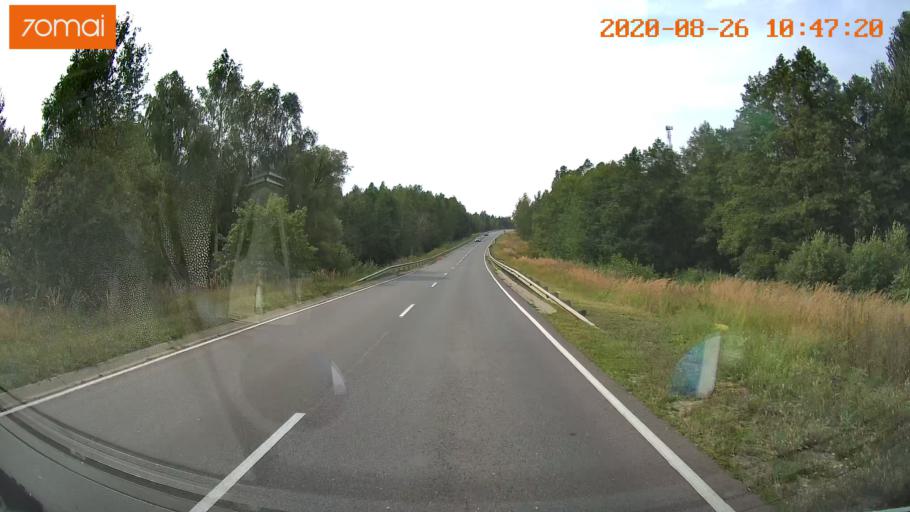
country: RU
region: Rjazan
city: Lashma
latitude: 54.7285
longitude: 41.1906
